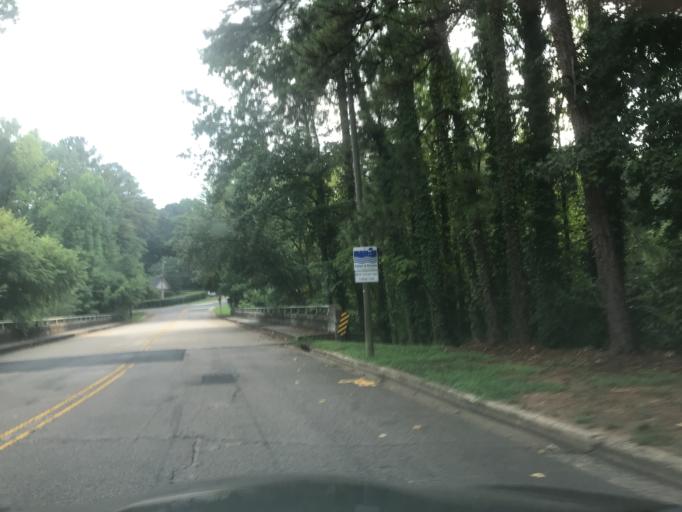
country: US
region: North Carolina
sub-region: Wake County
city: West Raleigh
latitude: 35.8348
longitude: -78.6584
